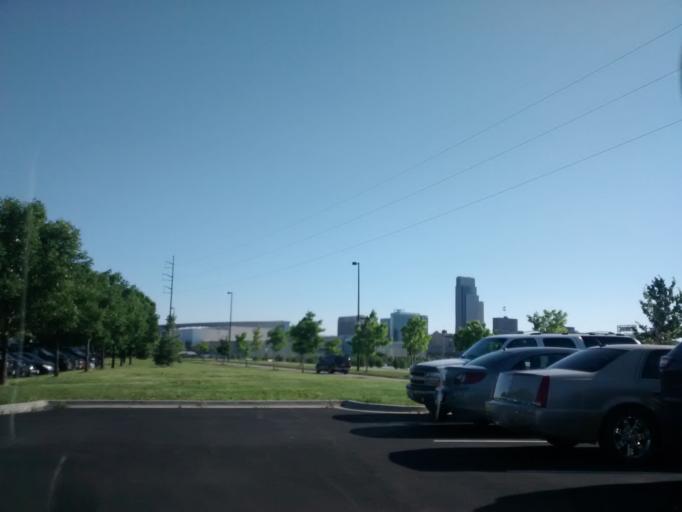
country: US
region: Nebraska
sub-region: Douglas County
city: Omaha
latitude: 41.2697
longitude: -95.9248
